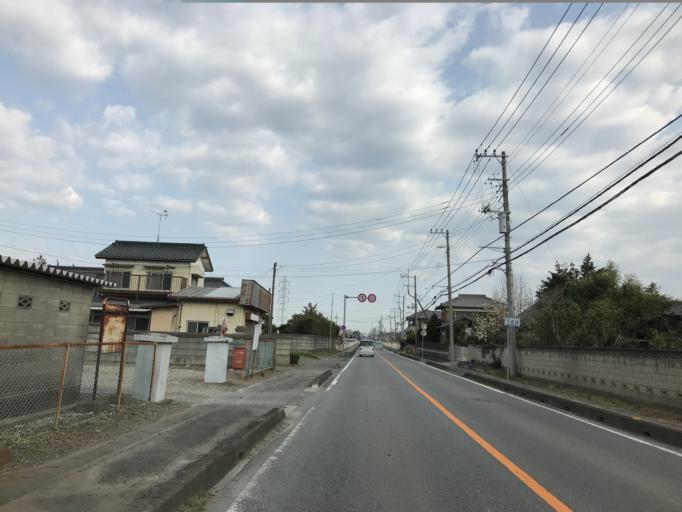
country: JP
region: Ibaraki
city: Mitsukaido
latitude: 36.0014
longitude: 140.0148
